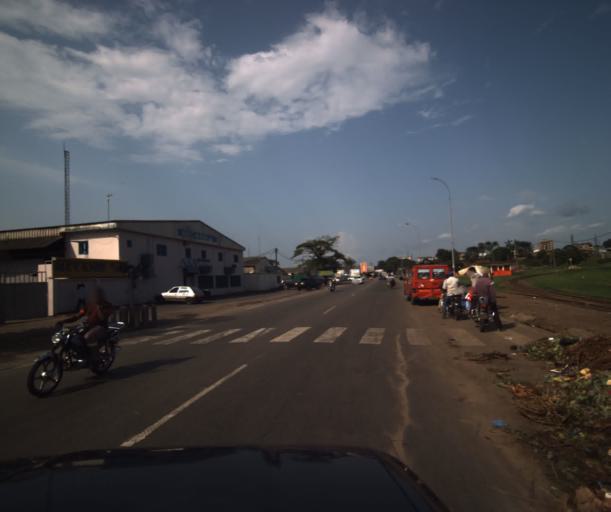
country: CM
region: Littoral
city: Douala
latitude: 4.0618
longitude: 9.7012
